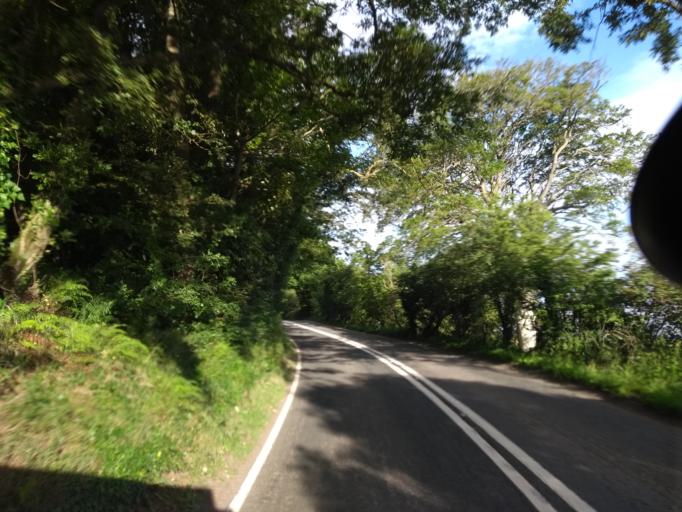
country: GB
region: England
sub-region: Somerset
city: Williton
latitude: 51.1754
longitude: -3.2627
